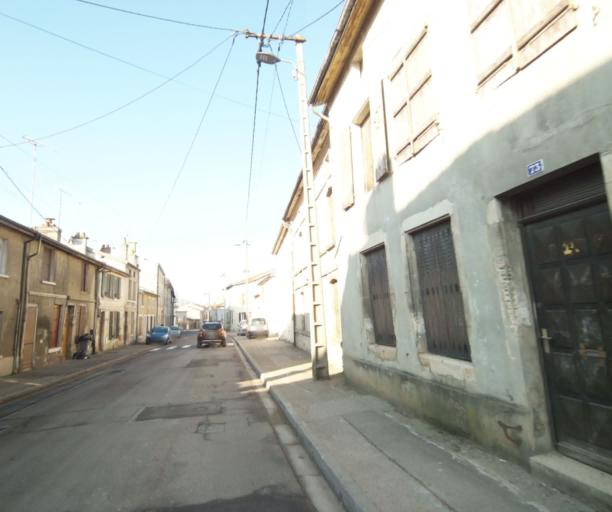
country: FR
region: Champagne-Ardenne
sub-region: Departement de la Haute-Marne
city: Wassy
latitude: 48.4956
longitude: 4.9520
